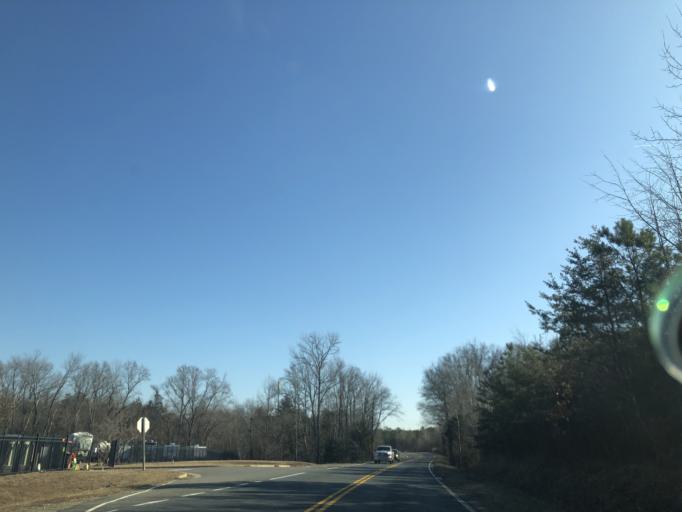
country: US
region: Virginia
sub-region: Spotsylvania County
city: Spotsylvania Courthouse
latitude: 38.1331
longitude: -77.5191
